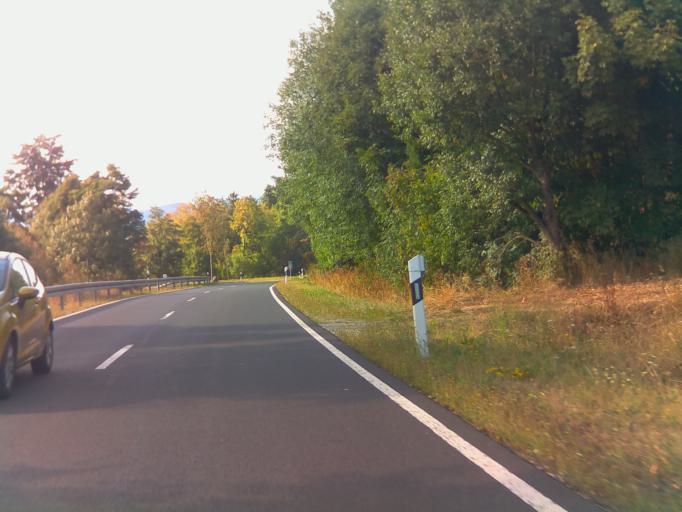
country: DE
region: Thuringia
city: Birx
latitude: 50.5125
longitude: 10.0375
